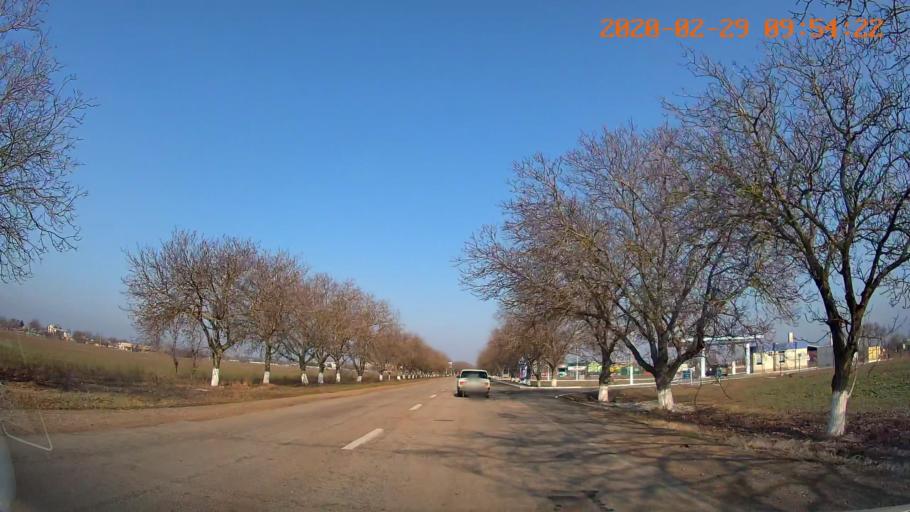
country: MD
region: Telenesti
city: Slobozia
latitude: 46.7281
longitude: 29.7163
